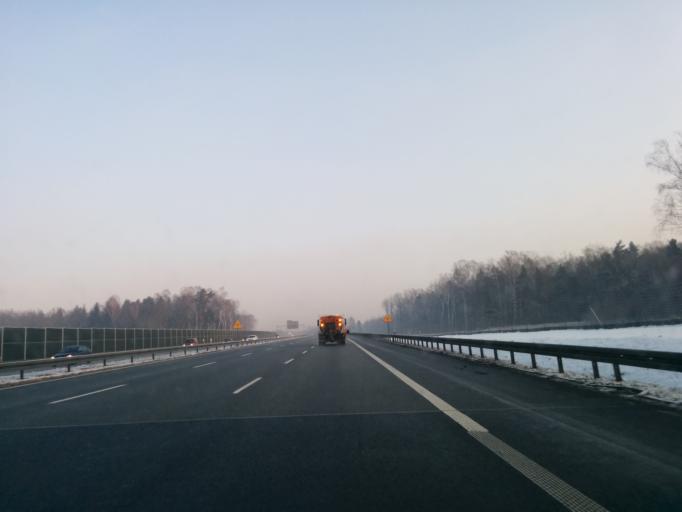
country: PL
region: Silesian Voivodeship
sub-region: Gliwice
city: Gliwice
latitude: 50.3196
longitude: 18.7267
